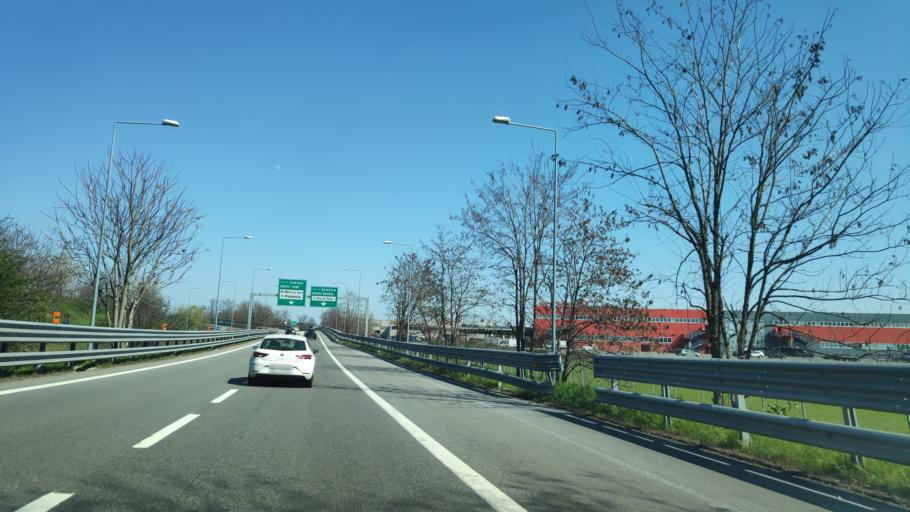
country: IT
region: Lombardy
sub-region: Provincia di Monza e Brianza
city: Agrate Brianza
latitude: 45.5647
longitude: 9.3390
